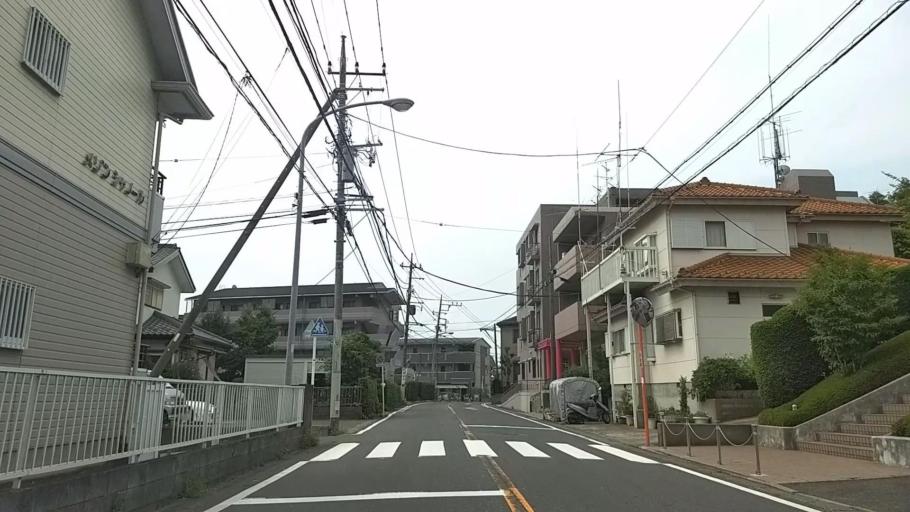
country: JP
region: Kanagawa
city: Yokohama
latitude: 35.5159
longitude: 139.5584
